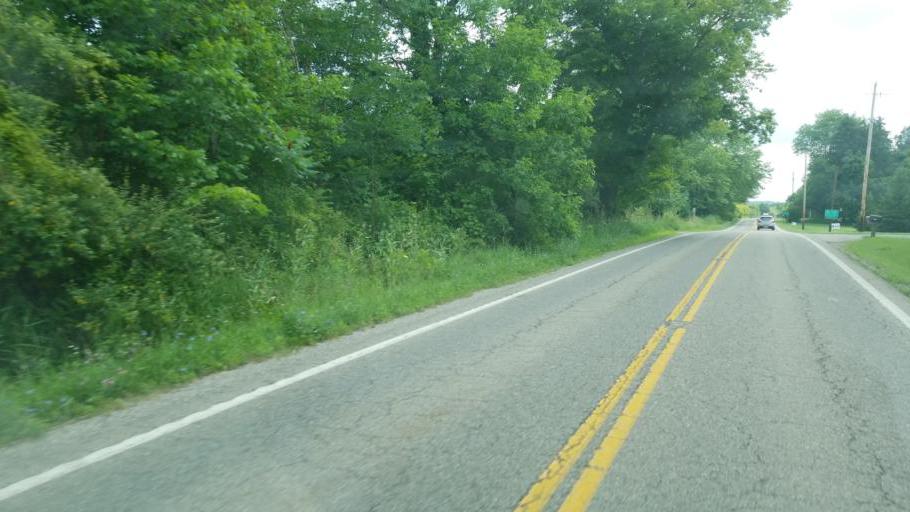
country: US
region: Ohio
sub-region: Columbiana County
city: New Waterford
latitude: 40.7964
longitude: -80.6662
